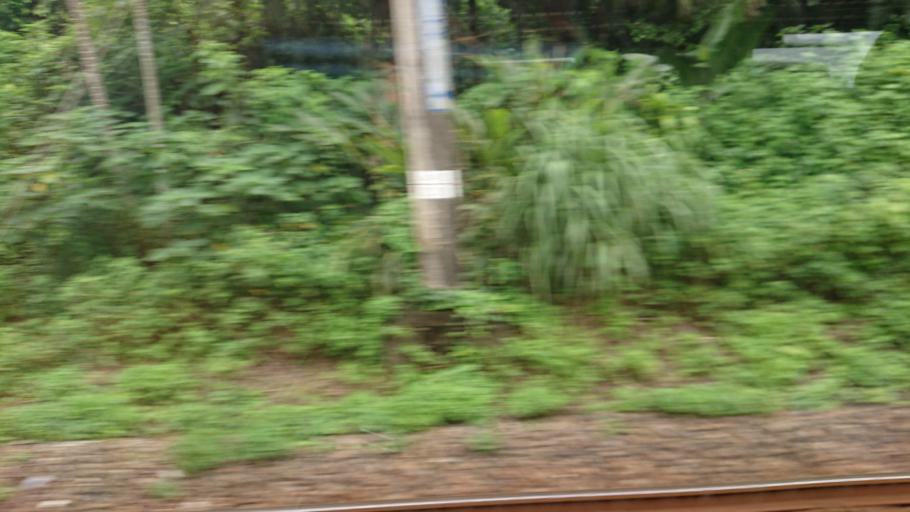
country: TW
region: Taiwan
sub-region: Yilan
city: Yilan
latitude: 24.9110
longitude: 121.8761
